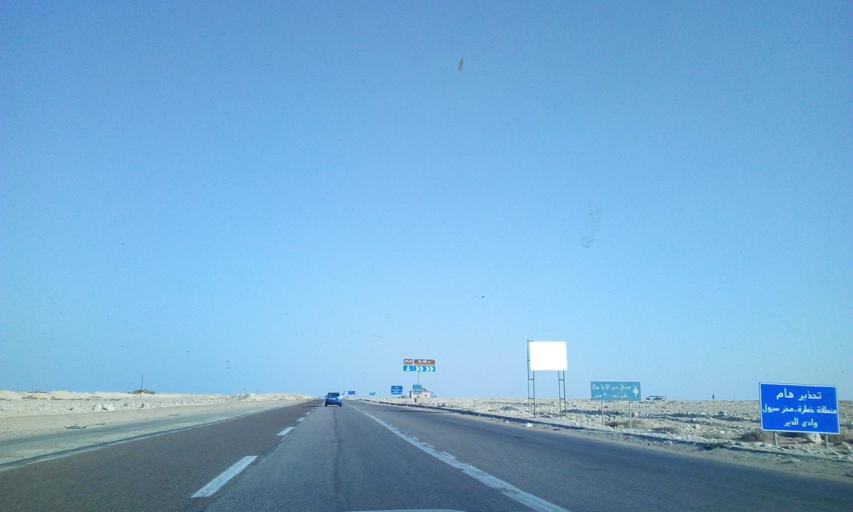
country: EG
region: As Suways
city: Ain Sukhna
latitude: 28.9000
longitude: 32.6354
